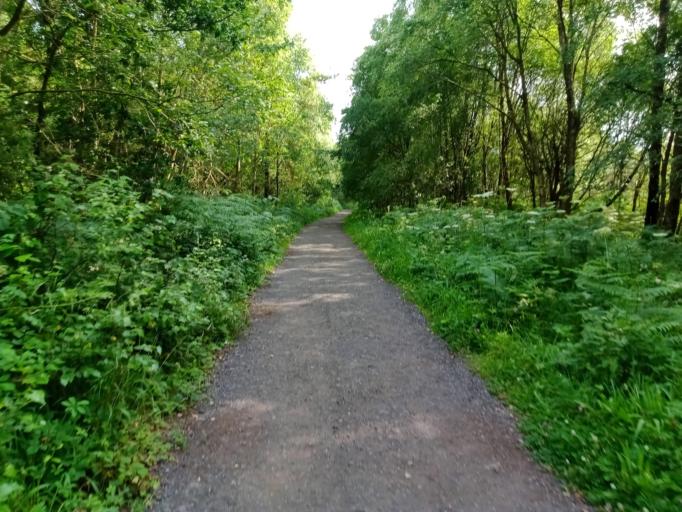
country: IE
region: Leinster
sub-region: Laois
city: Abbeyleix
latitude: 52.9001
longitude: -7.3503
